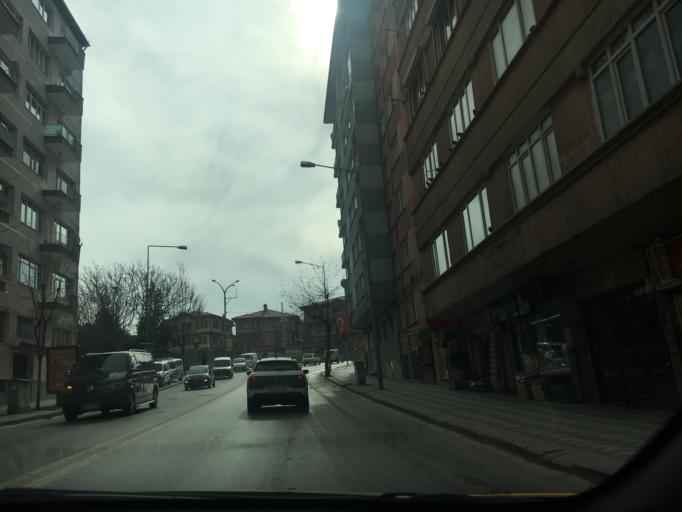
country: TR
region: Eskisehir
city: Eskisehir
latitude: 39.7661
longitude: 30.5203
